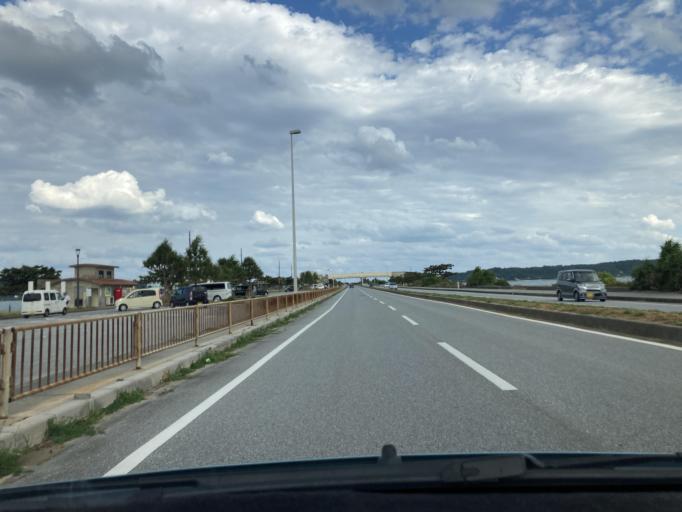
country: JP
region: Okinawa
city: Katsuren-haebaru
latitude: 26.3316
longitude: 127.9258
